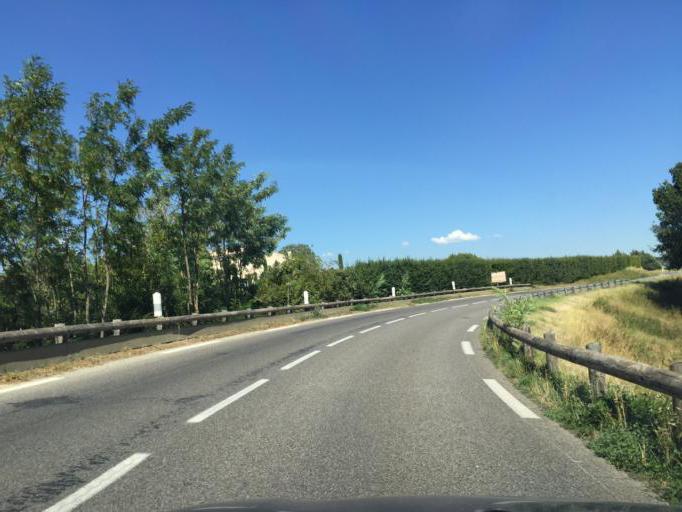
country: FR
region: Provence-Alpes-Cote d'Azur
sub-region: Departement des Alpes-de-Haute-Provence
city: Mane
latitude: 43.9214
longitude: 5.7566
